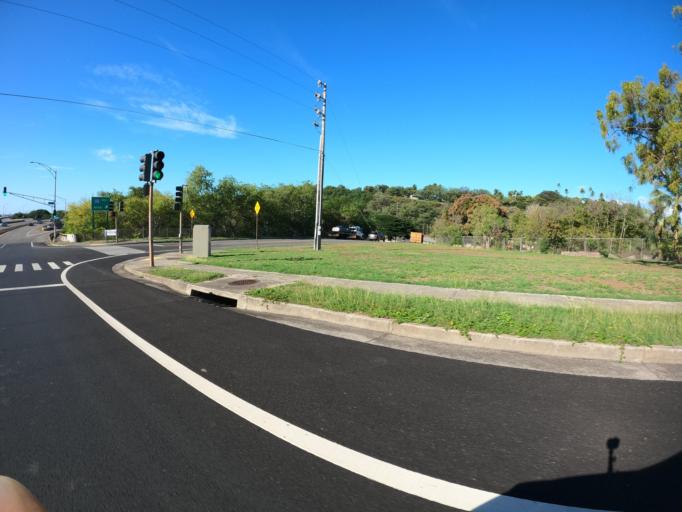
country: US
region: Hawaii
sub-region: Honolulu County
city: Halawa Heights
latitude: 21.3516
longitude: -157.8944
